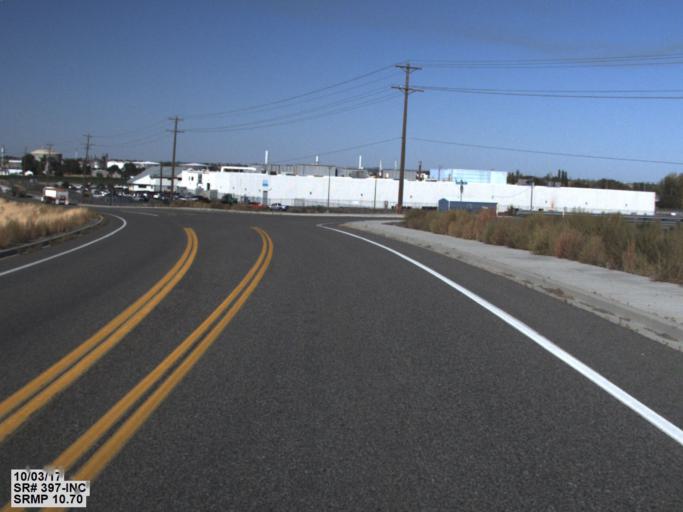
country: US
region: Washington
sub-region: Benton County
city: Finley
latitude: 46.1424
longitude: -119.0131
